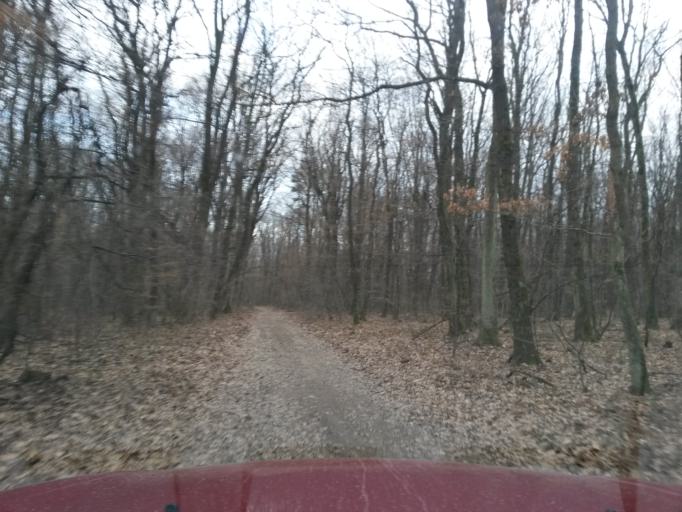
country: SK
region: Kosicky
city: Kosice
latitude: 48.7001
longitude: 21.2972
